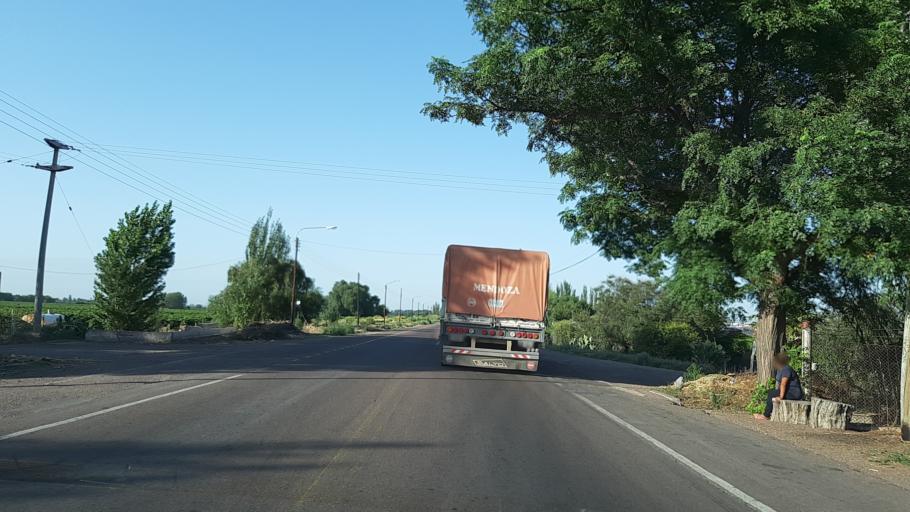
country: AR
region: Mendoza
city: San Martin
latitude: -32.9881
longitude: -68.4670
